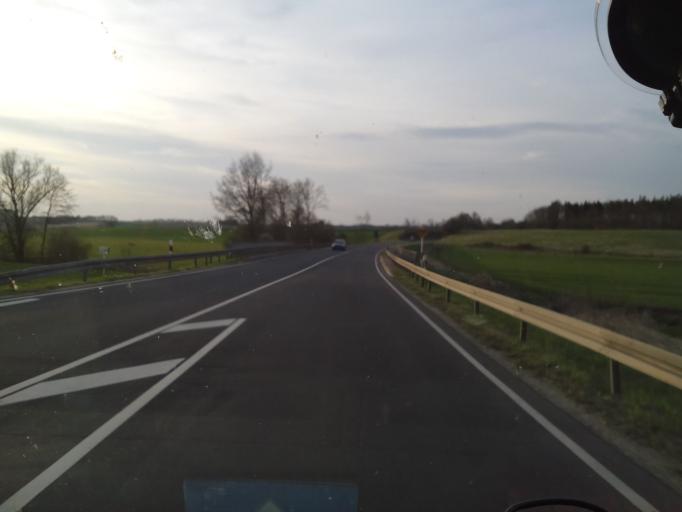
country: DE
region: Bavaria
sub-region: Regierungsbezirk Unterfranken
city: Pfarrweisach
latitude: 50.1173
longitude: 10.7662
